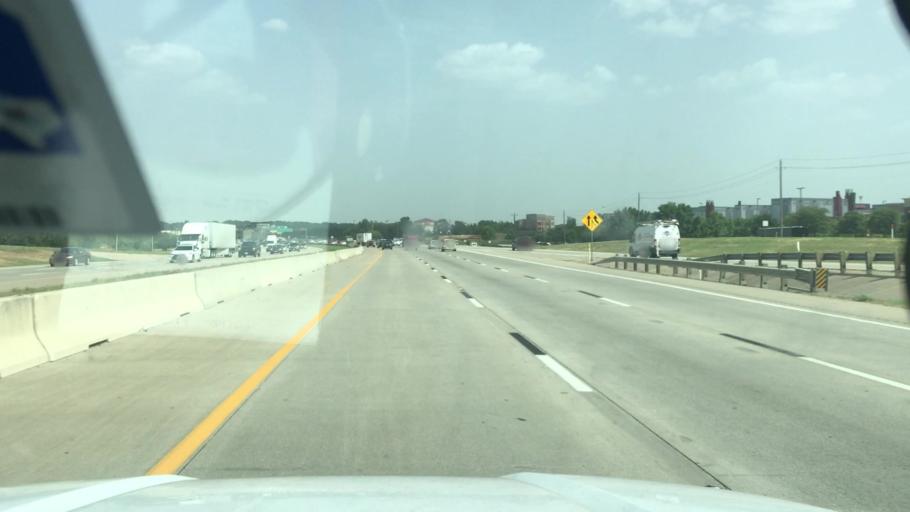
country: US
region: Texas
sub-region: Tarrant County
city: Southlake
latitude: 32.9482
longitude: -97.1297
